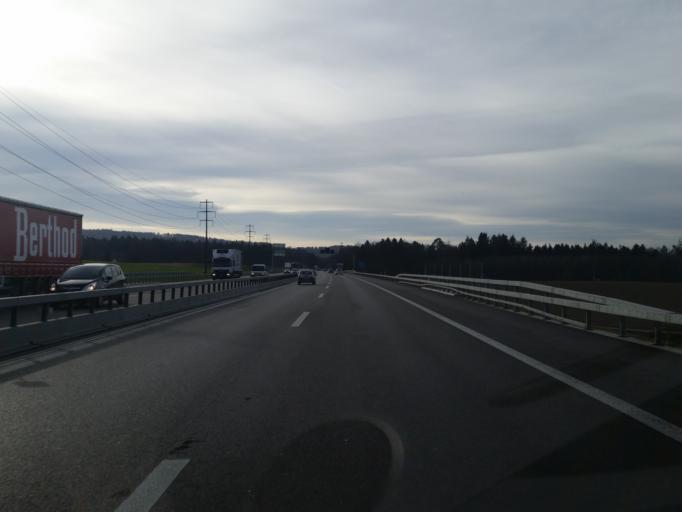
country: CH
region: Aargau
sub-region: Bezirk Baden
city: Birmenstorf
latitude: 47.4379
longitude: 8.2404
